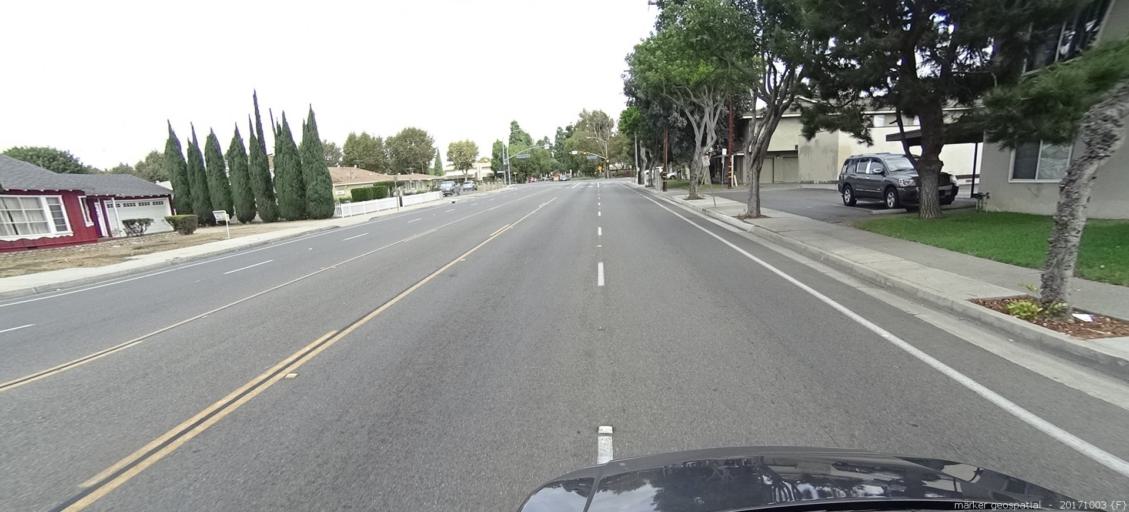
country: US
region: California
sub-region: Orange County
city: Garden Grove
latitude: 33.7732
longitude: -117.9291
